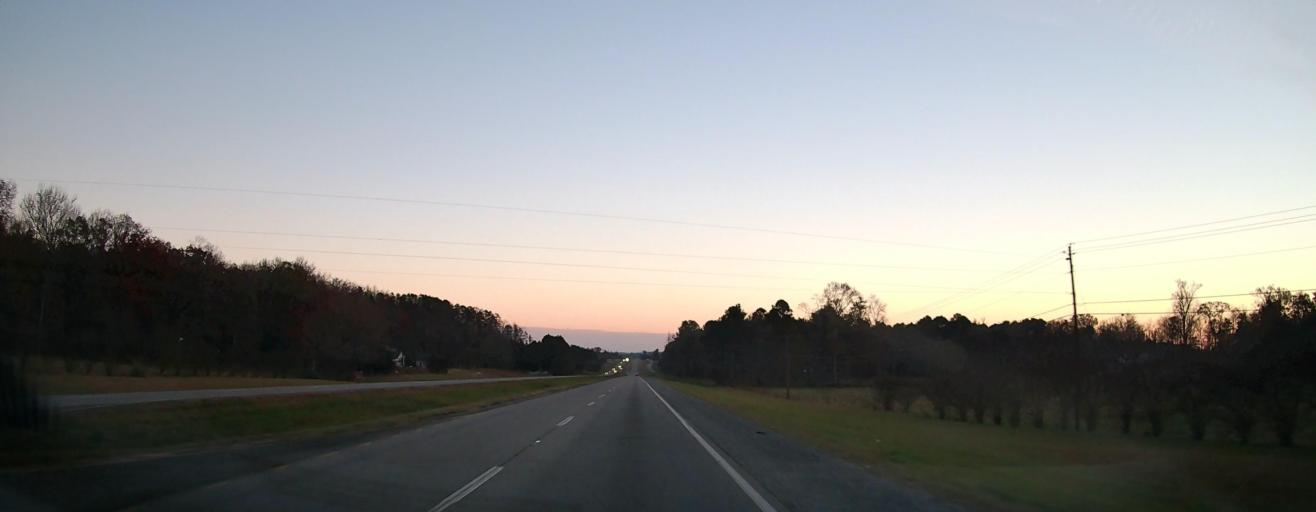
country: US
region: Alabama
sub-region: Calhoun County
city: Alexandria
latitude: 33.8357
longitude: -85.9137
